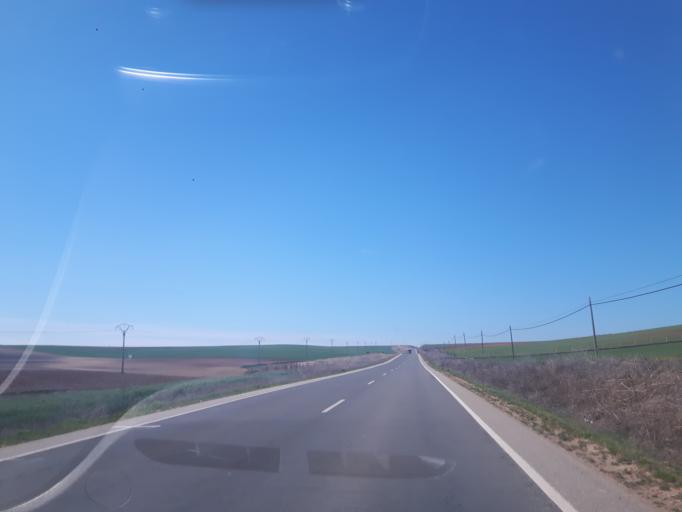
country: ES
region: Castille and Leon
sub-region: Provincia de Salamanca
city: Aldeaseca de Alba
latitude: 40.8366
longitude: -5.4765
